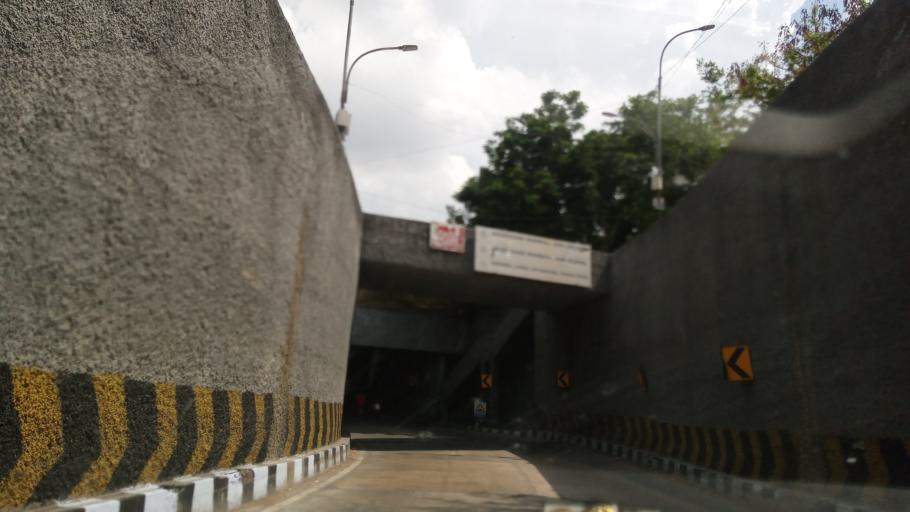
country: IN
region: Tamil Nadu
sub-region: Kancheepuram
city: Saint Thomas Mount
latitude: 12.9848
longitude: 80.1768
